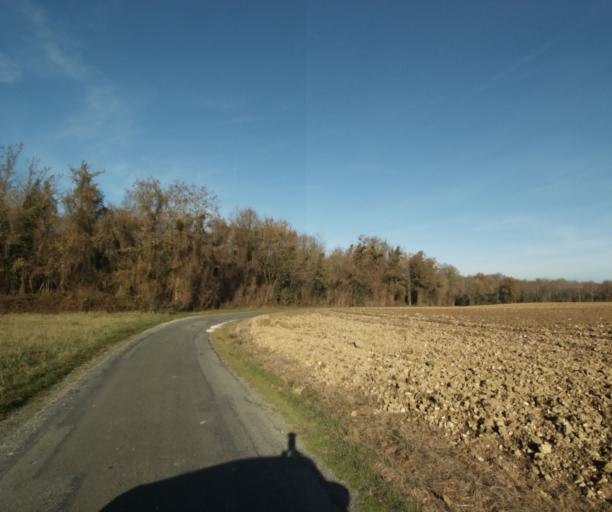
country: FR
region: Poitou-Charentes
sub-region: Departement de la Charente-Maritime
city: Chaniers
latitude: 45.7594
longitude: -0.5102
